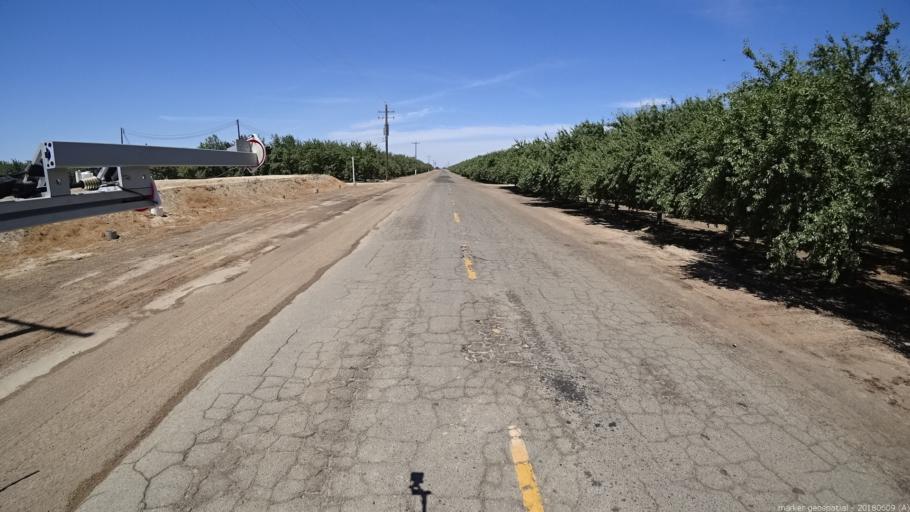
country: US
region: California
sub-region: Madera County
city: Fairmead
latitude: 36.9382
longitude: -120.2328
